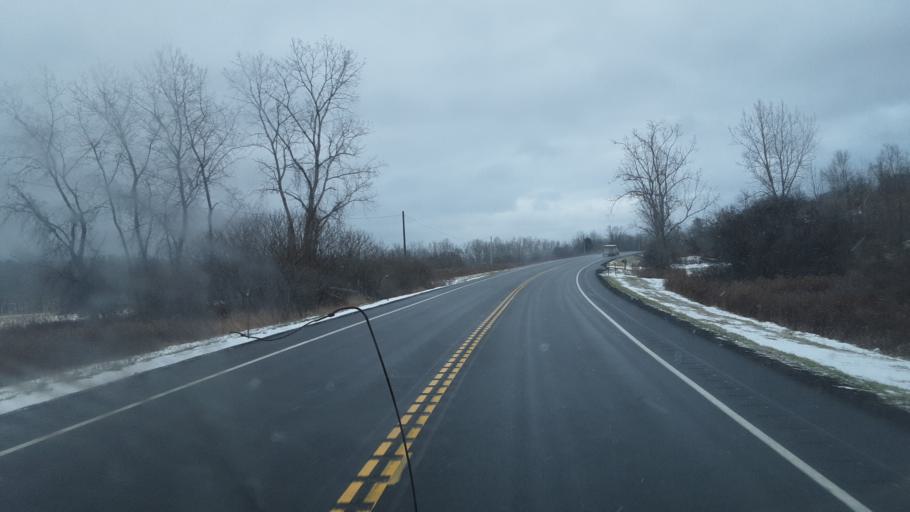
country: US
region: New York
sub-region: Allegany County
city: Belmont
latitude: 42.2865
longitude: -78.0651
